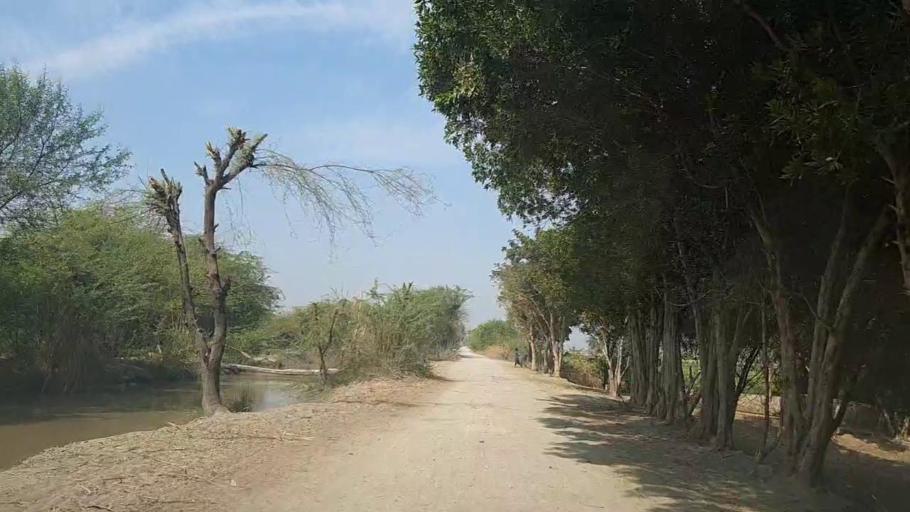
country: PK
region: Sindh
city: Mirpur Khas
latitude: 25.4839
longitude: 68.9280
